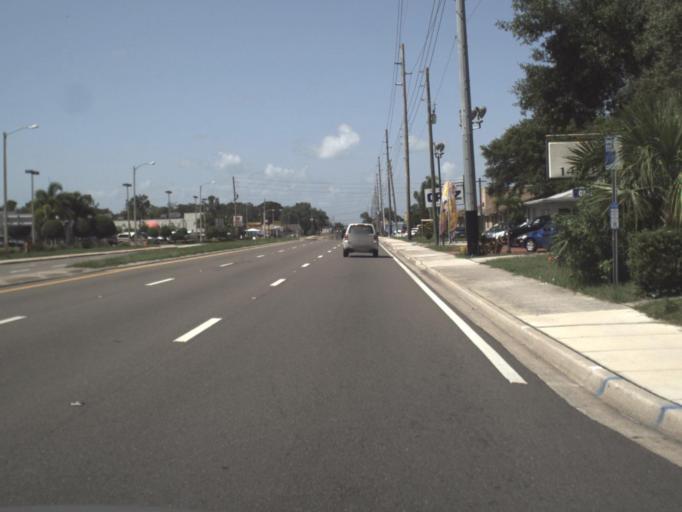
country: US
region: Florida
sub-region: Pinellas County
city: Belleair
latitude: 27.9426
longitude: -82.7873
